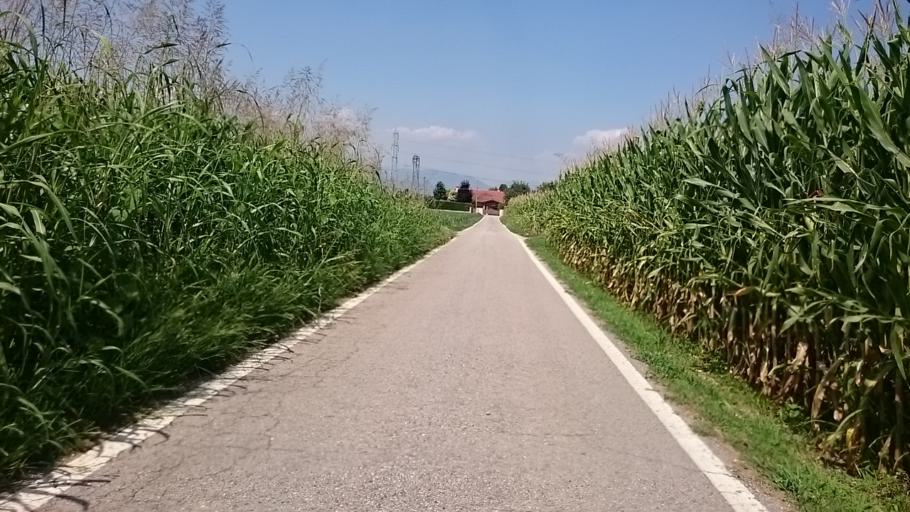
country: IT
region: Veneto
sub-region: Provincia di Padova
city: Fontaniva
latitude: 45.6662
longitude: 11.7492
